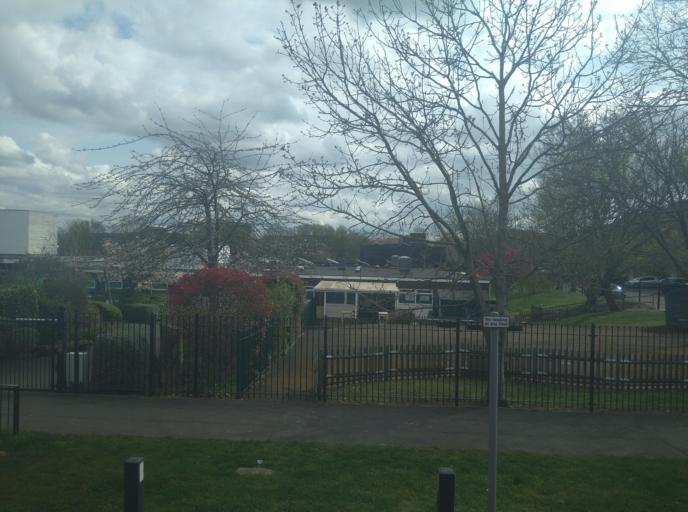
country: GB
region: England
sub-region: Greater London
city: Purley
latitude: 51.3562
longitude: -0.1286
